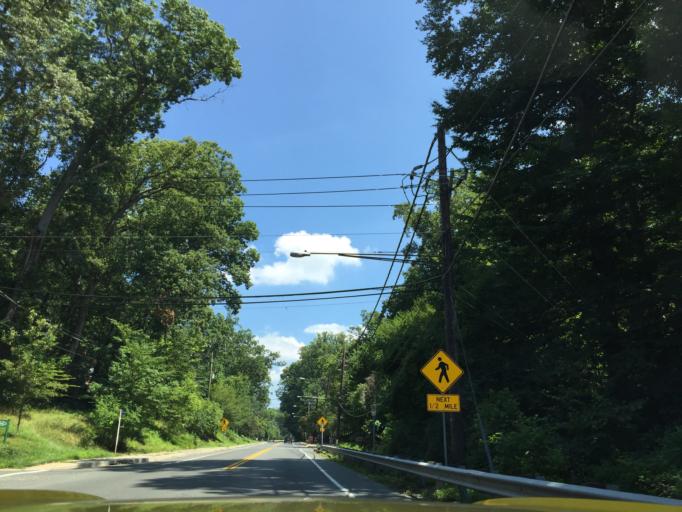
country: US
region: Maryland
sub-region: Montgomery County
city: Cabin John
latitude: 38.9693
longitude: -77.1303
